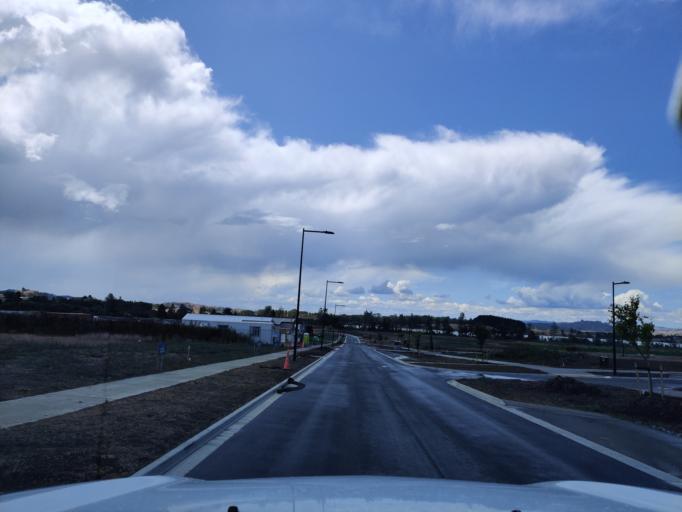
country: NZ
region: Waikato
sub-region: Waikato District
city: Te Kauwhata
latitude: -37.4131
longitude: 175.1500
